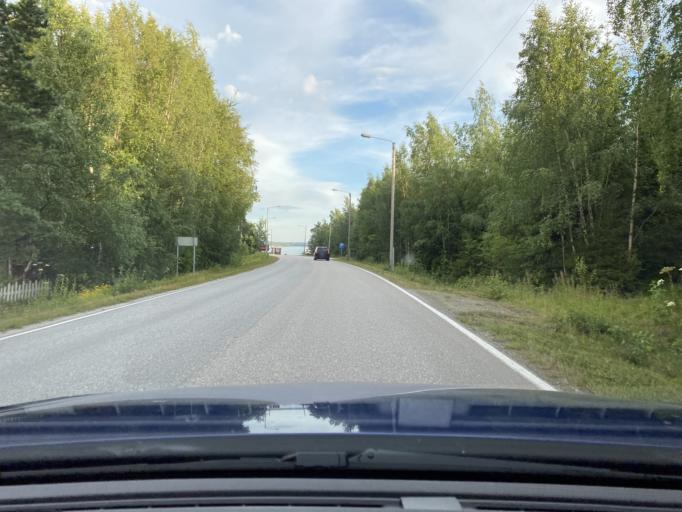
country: FI
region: Ostrobothnia
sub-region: Vaasa
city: Korsnaes
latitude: 62.9459
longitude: 21.1757
